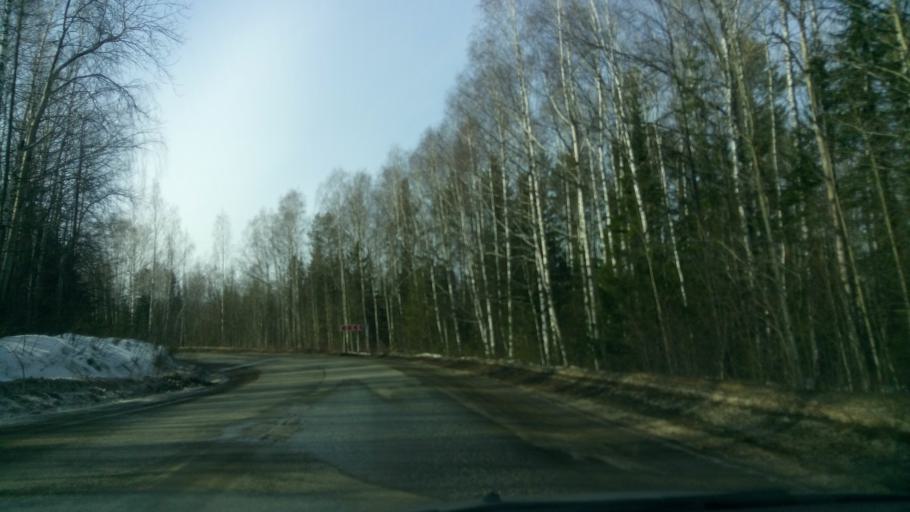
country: RU
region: Sverdlovsk
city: Uralets
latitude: 57.6967
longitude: 59.7590
